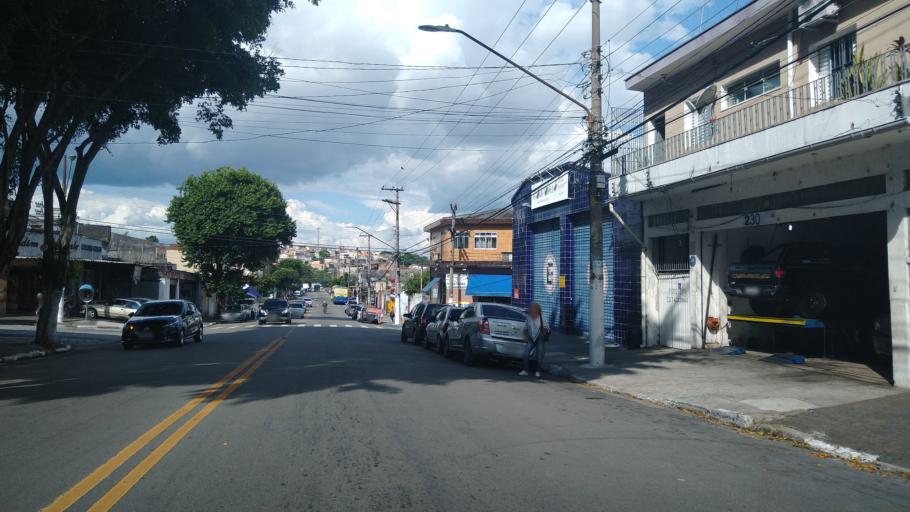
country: BR
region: Sao Paulo
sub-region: Osasco
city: Osasco
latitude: -23.5133
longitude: -46.7770
